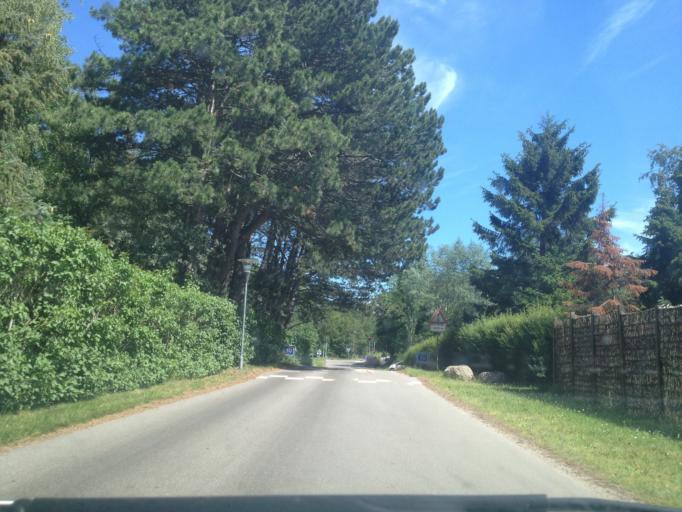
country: DK
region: Zealand
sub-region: Odsherred Kommune
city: Hojby
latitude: 55.9114
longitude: 11.5455
